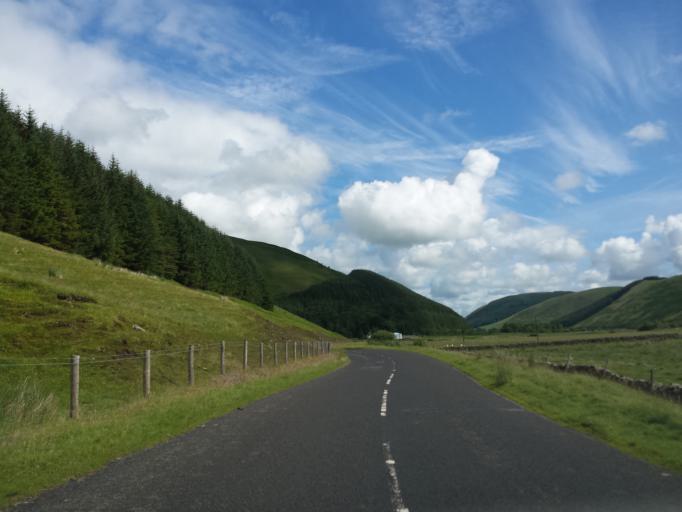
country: GB
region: Scotland
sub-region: The Scottish Borders
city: Peebles
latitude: 55.4531
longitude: -3.2215
